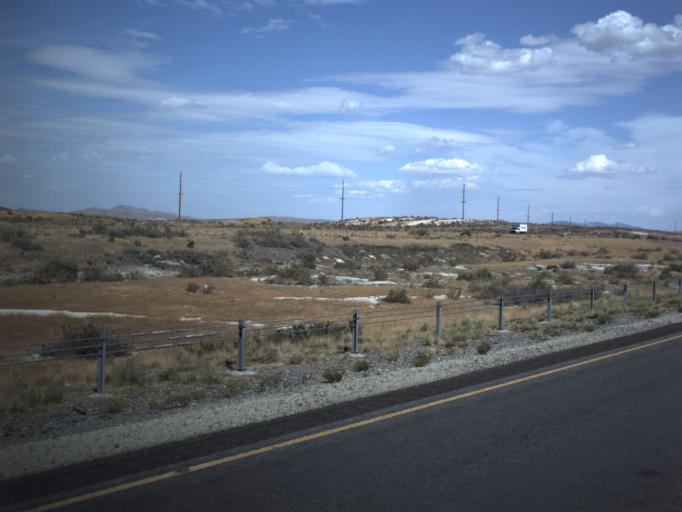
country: US
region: Utah
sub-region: Tooele County
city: Grantsville
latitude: 40.7252
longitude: -113.1403
